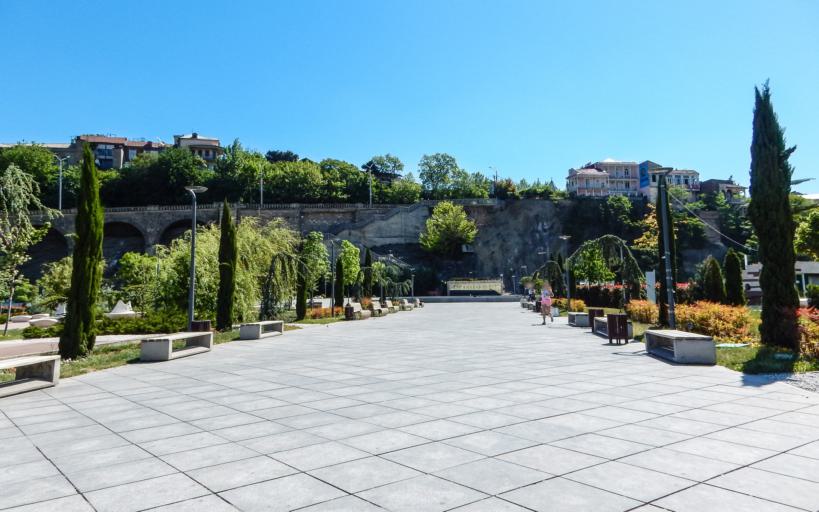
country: GE
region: T'bilisi
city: Tbilisi
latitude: 41.6930
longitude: 44.8099
